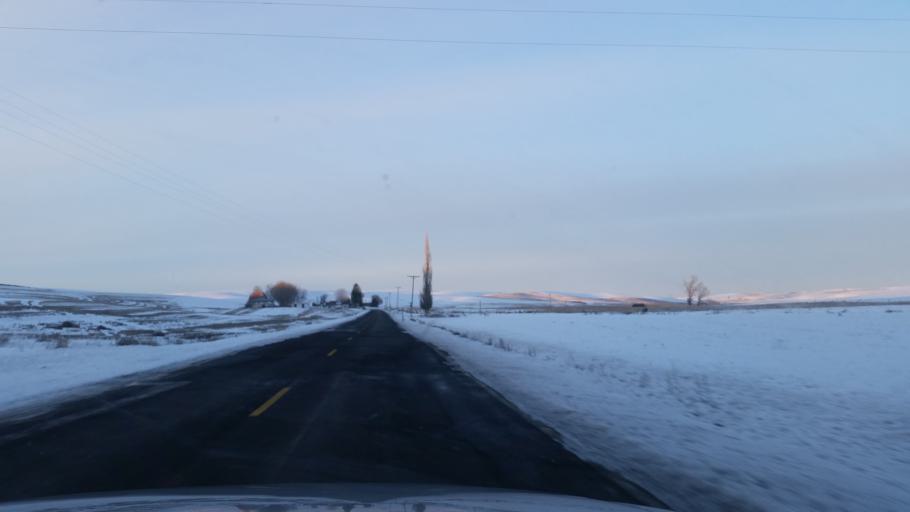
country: US
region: Washington
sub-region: Spokane County
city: Cheney
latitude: 47.1335
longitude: -117.8294
